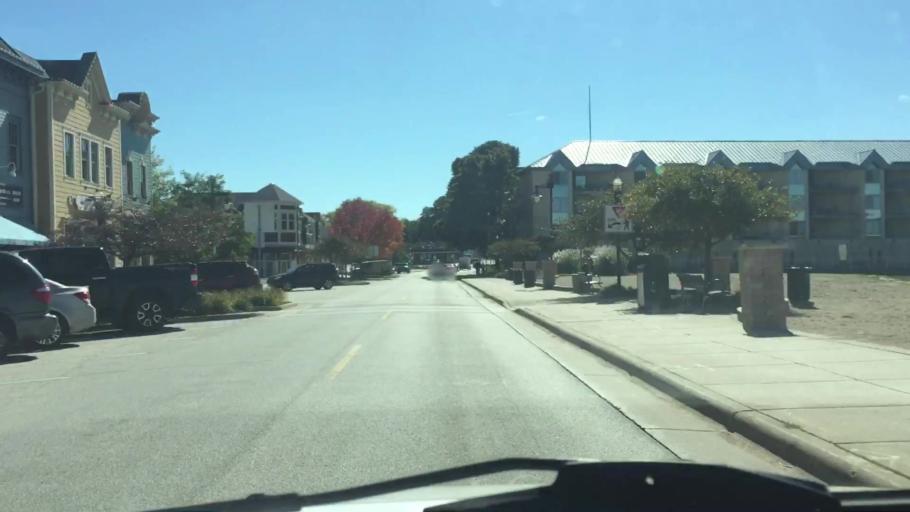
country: US
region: Wisconsin
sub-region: Waukesha County
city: Pewaukee
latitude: 43.0839
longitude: -88.2641
